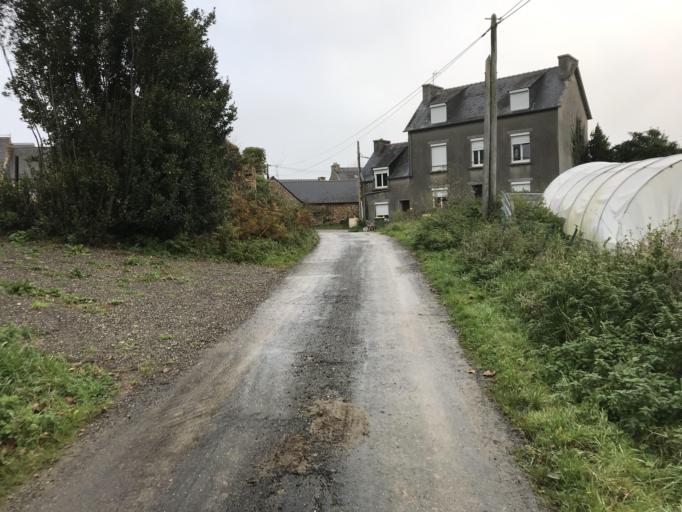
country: FR
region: Brittany
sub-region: Departement du Finistere
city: Logonna-Daoulas
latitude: 48.3393
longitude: -4.2778
